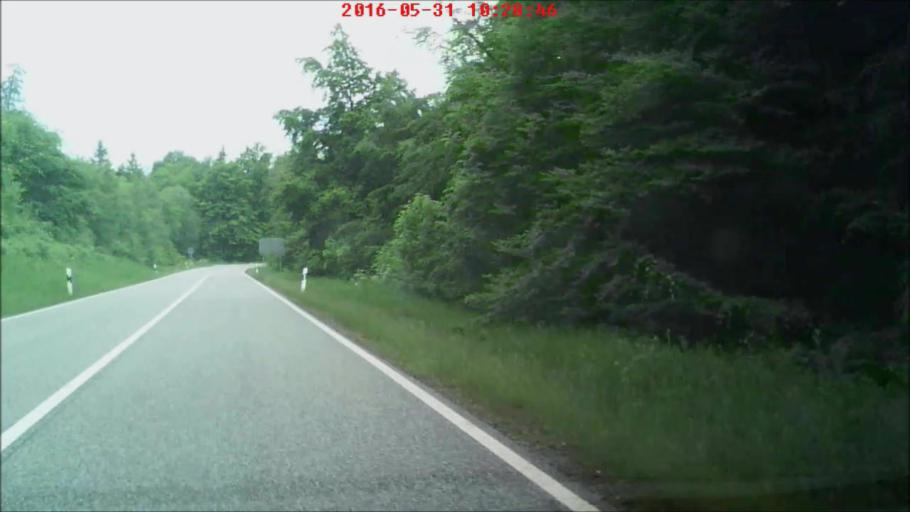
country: DE
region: Saxony-Anhalt
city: Kelbra
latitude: 51.4117
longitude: 11.0800
